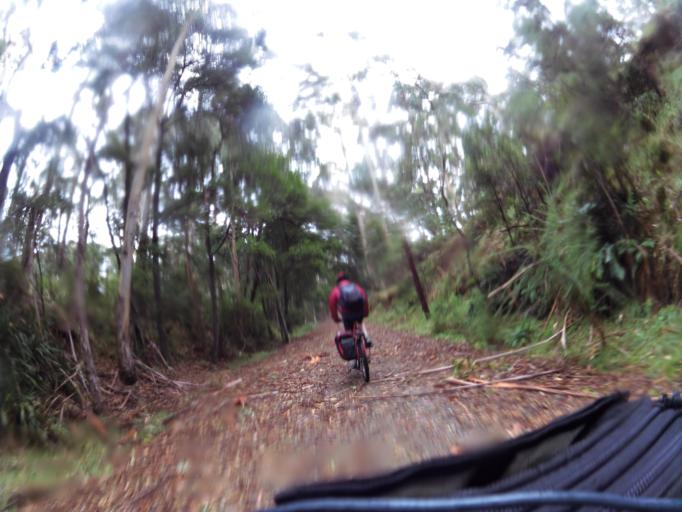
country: AU
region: New South Wales
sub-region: Greater Hume Shire
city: Holbrook
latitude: -36.1901
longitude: 147.5068
